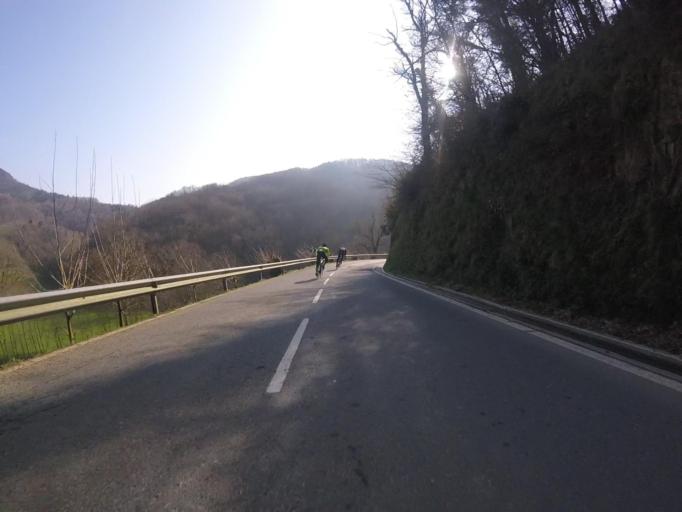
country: ES
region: Navarre
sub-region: Provincia de Navarra
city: Bera
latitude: 43.2900
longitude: -1.6808
